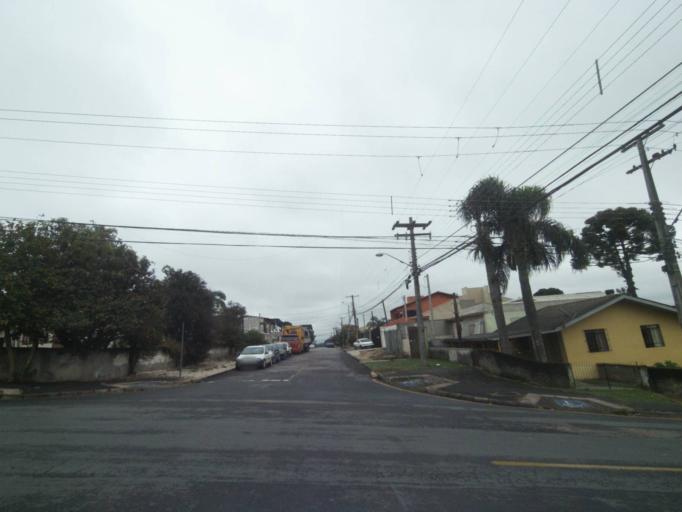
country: BR
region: Parana
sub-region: Curitiba
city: Curitiba
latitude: -25.5162
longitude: -49.3043
